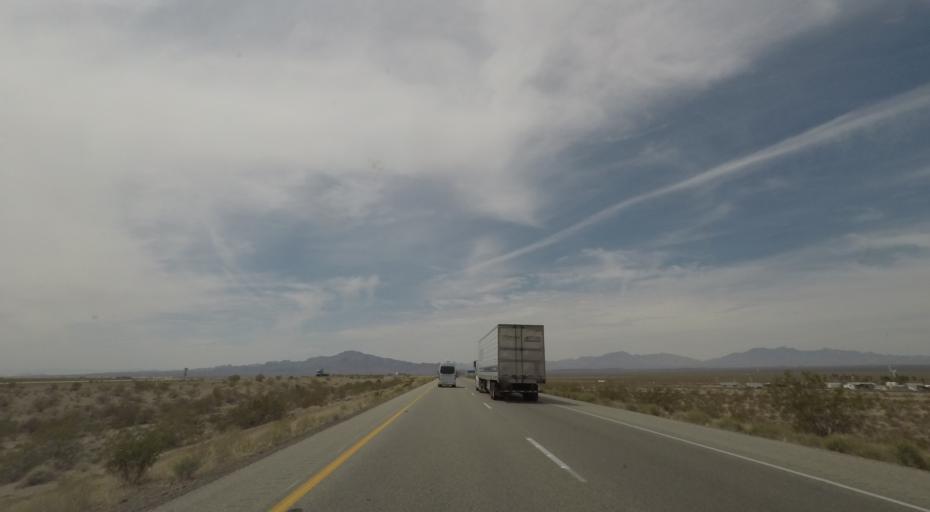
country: US
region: California
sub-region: San Bernardino County
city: Needles
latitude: 34.8142
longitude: -115.1766
